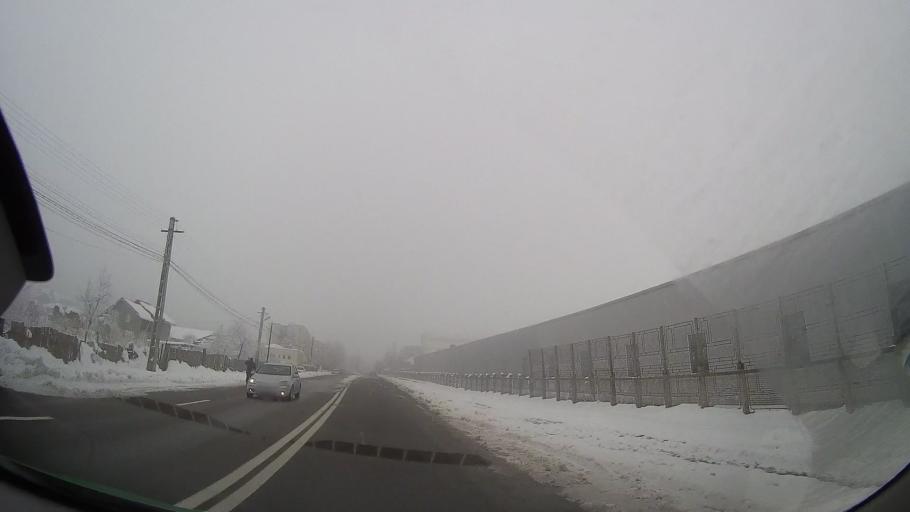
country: RO
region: Iasi
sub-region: Municipiul Pascani
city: Pascani
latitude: 47.2392
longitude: 26.7291
